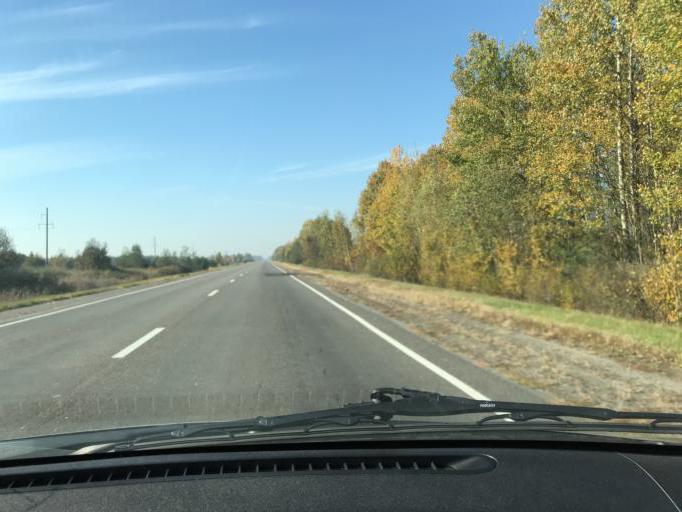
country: BY
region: Brest
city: Horad Luninyets
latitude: 52.3109
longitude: 26.5349
